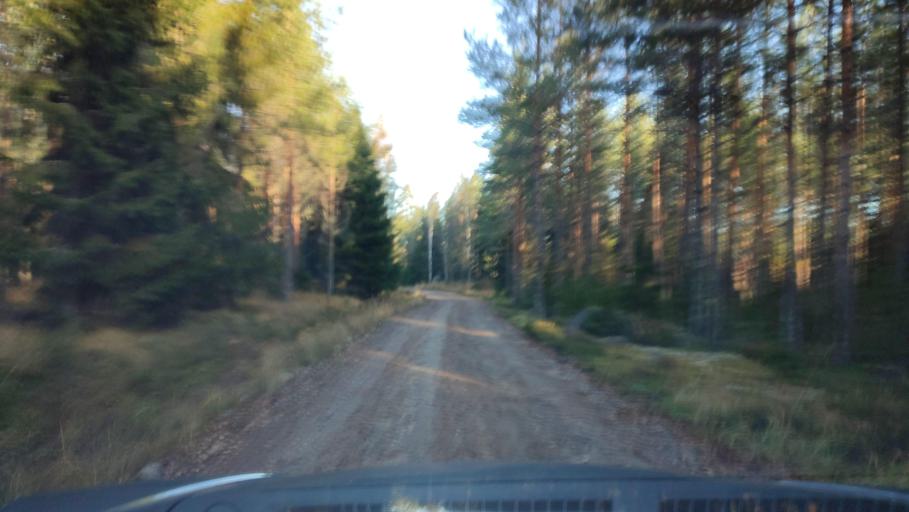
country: FI
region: Southern Ostrobothnia
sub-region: Suupohja
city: Karijoki
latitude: 62.2146
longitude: 21.6277
